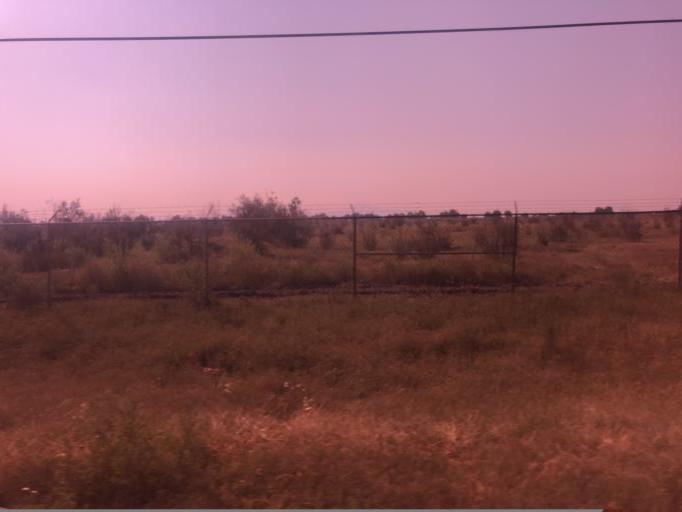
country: MX
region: Mexico
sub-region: Ciudad Nezahualcoyotl
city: Poligonos
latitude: 19.4758
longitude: -98.9858
